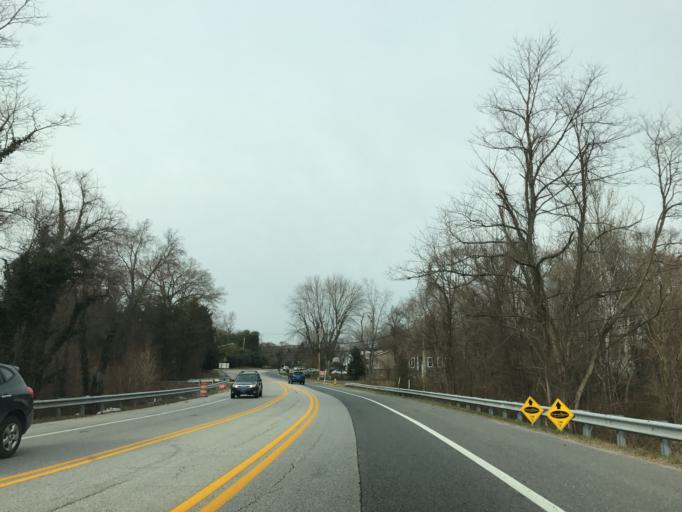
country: US
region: Maryland
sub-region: Anne Arundel County
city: Severna Park
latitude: 39.0945
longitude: -76.5478
